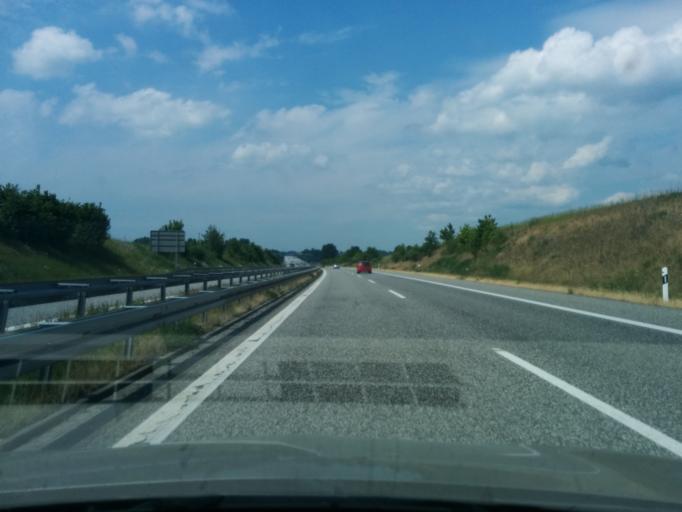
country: DE
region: Mecklenburg-Vorpommern
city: Pasewalk
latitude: 53.4735
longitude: 13.9534
